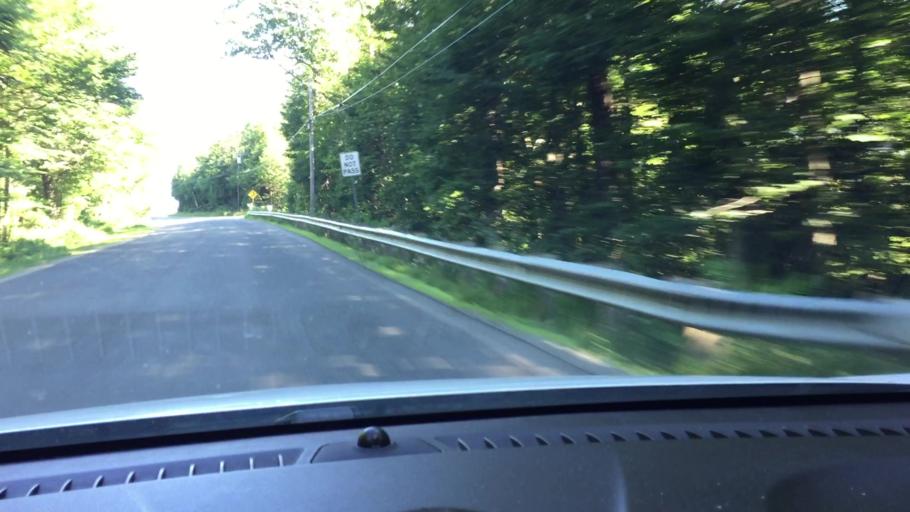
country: US
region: Massachusetts
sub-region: Berkshire County
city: Hinsdale
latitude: 42.4486
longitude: -72.9781
